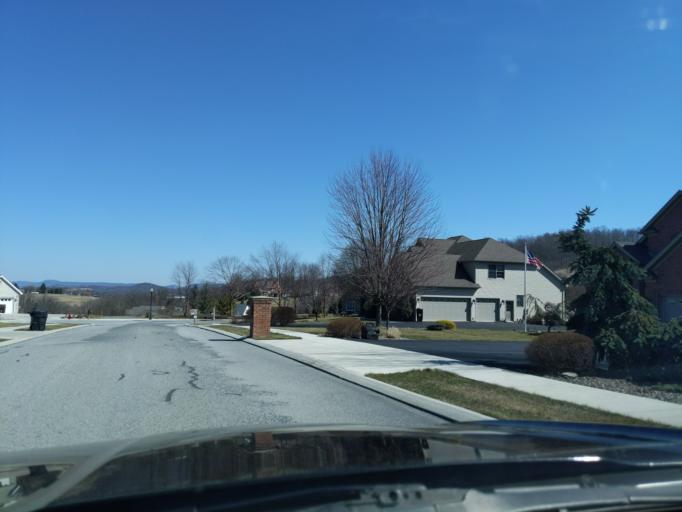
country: US
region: Pennsylvania
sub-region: Blair County
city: Duncansville
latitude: 40.4111
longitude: -78.4215
